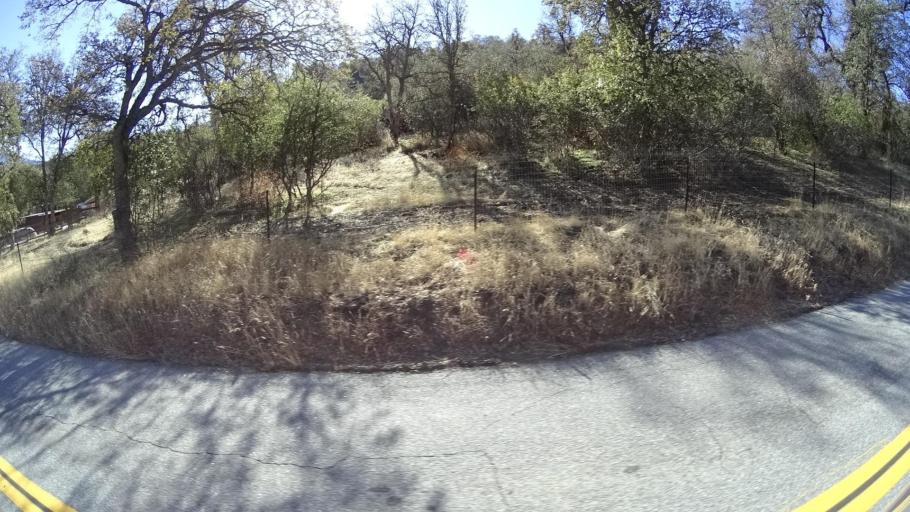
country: US
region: California
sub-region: Kern County
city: Alta Sierra
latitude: 35.7922
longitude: -118.7321
